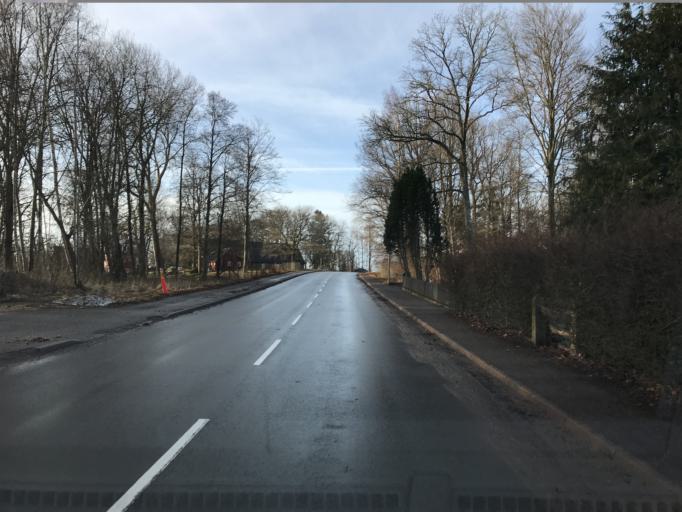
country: SE
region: Skane
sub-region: Hassleholms Kommun
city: Bjarnum
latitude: 56.2953
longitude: 13.7225
